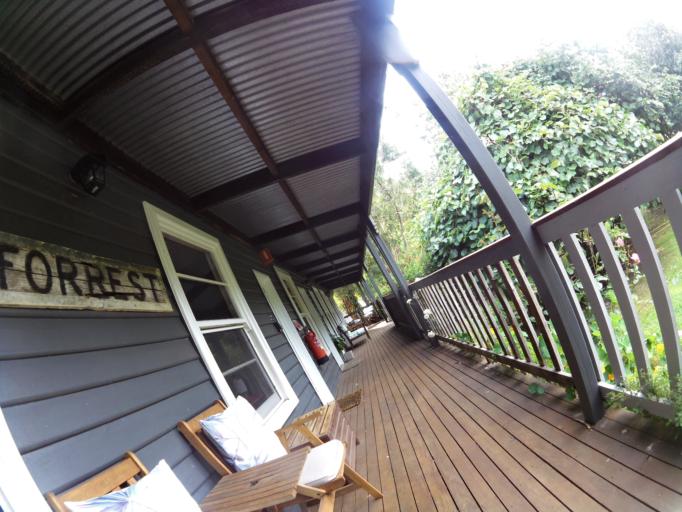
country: AU
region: Victoria
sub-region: Colac-Otway
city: Colac
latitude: -38.5172
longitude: 143.7144
